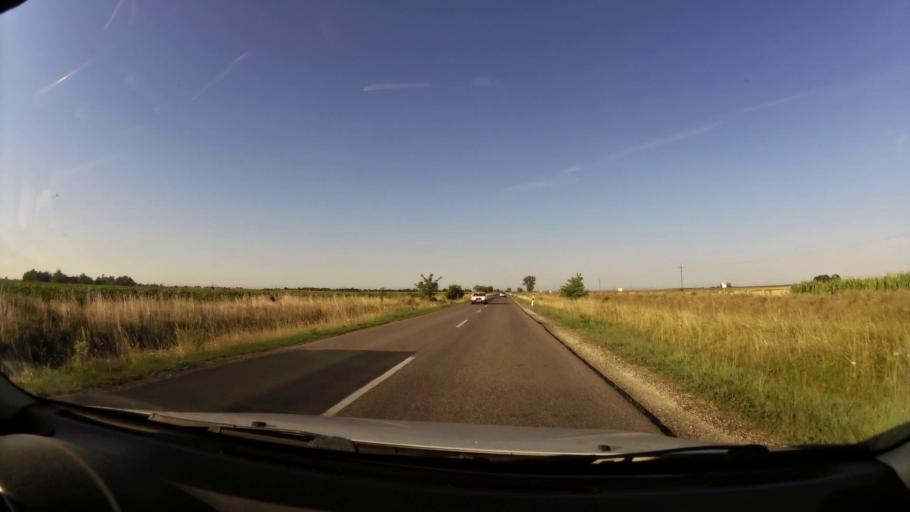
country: HU
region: Pest
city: Tapioszolos
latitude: 47.2587
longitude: 19.8540
